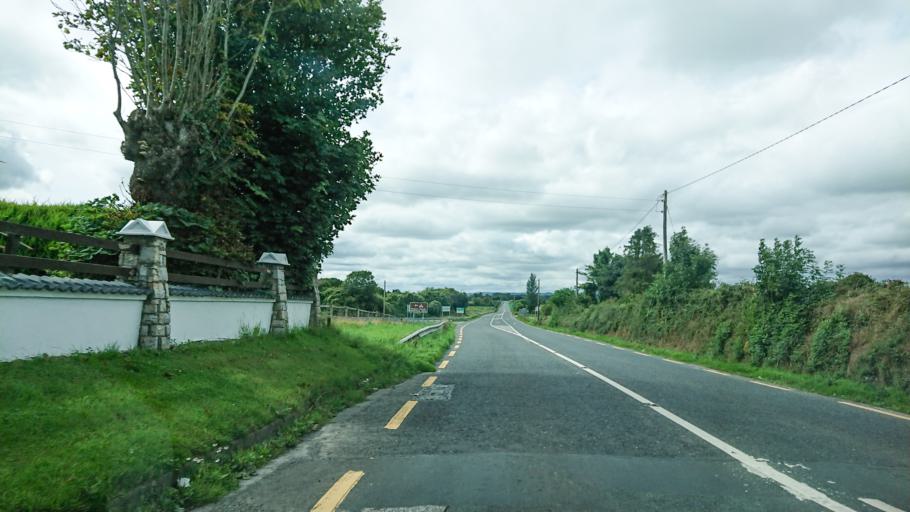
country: IE
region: Munster
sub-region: Waterford
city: Dungarvan
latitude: 52.1246
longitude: -7.7715
